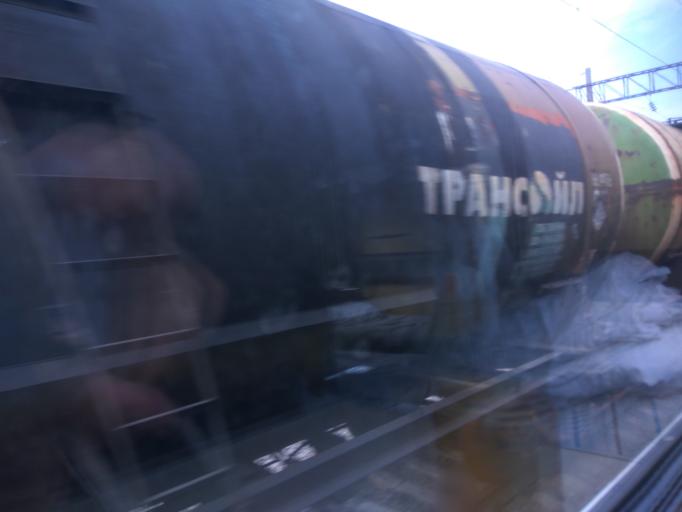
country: RU
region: Saratov
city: Rtishchevo
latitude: 52.2076
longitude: 43.8862
